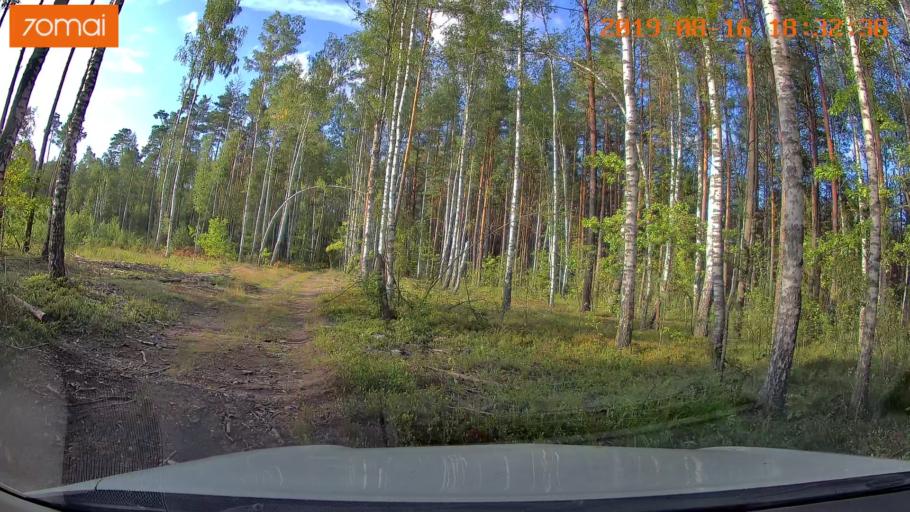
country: BY
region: Mogilev
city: Asipovichy
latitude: 53.2000
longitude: 28.6393
